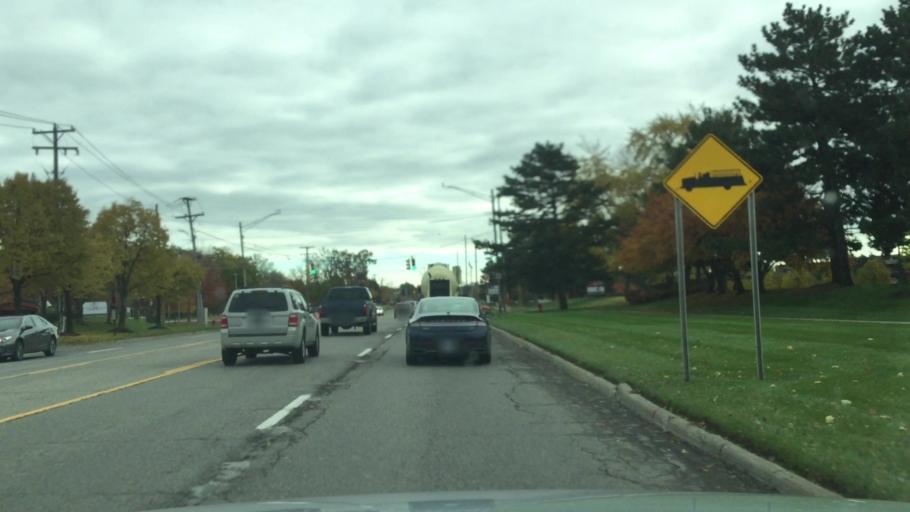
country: US
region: Michigan
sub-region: Oakland County
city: Franklin
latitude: 42.5009
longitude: -83.2939
